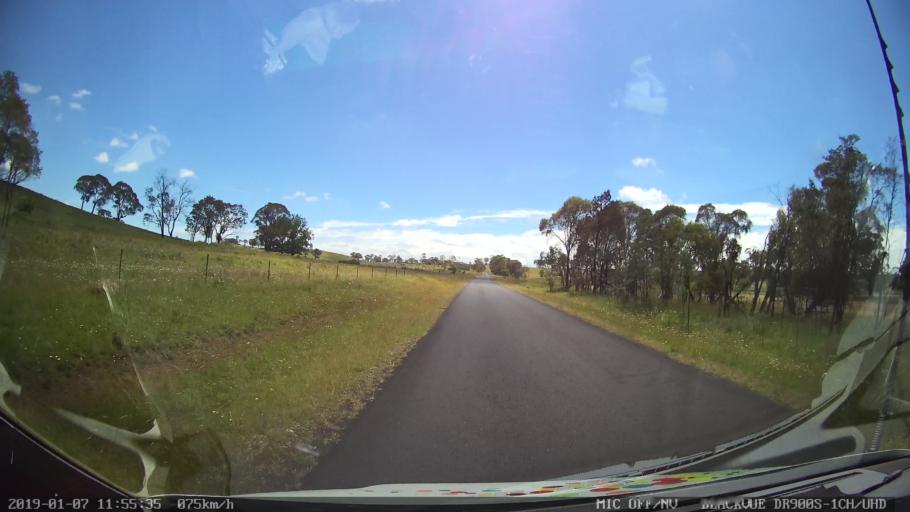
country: AU
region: New South Wales
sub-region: Guyra
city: Guyra
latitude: -30.2838
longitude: 151.6706
